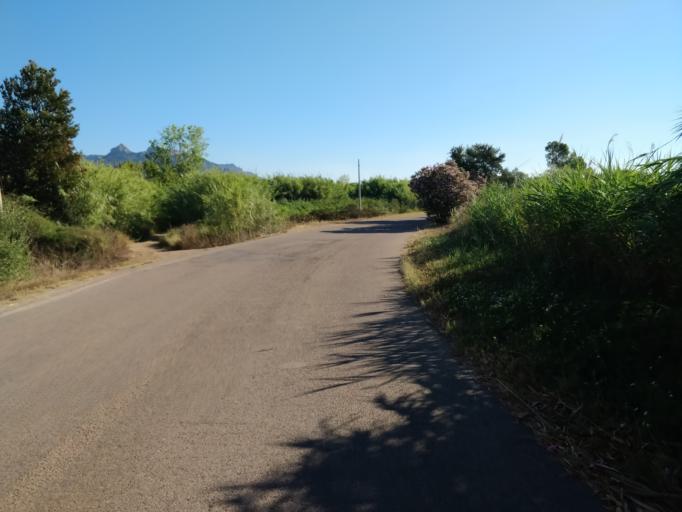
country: IT
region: Sardinia
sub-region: Provincia di Ogliastra
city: Girasole
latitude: 39.9542
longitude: 9.6716
